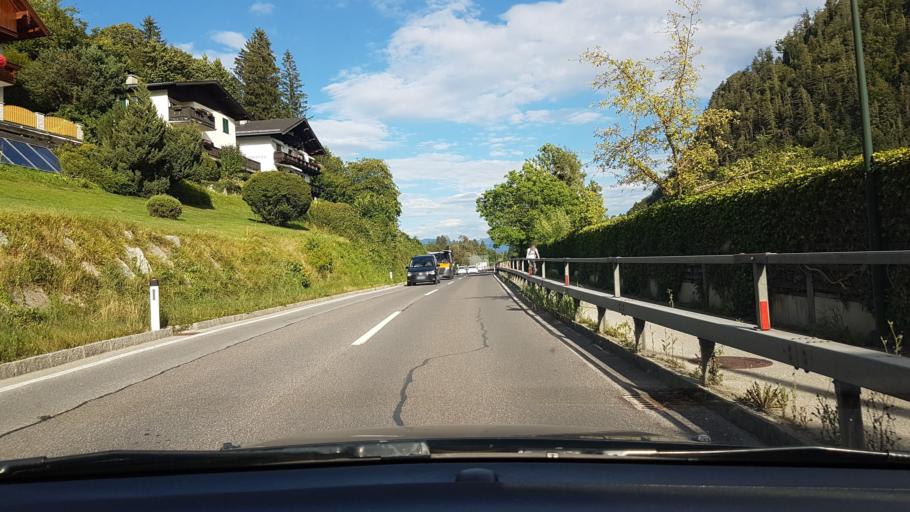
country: AT
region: Salzburg
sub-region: Politischer Bezirk Salzburg-Umgebung
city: Strobl
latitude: 47.7306
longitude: 13.4790
